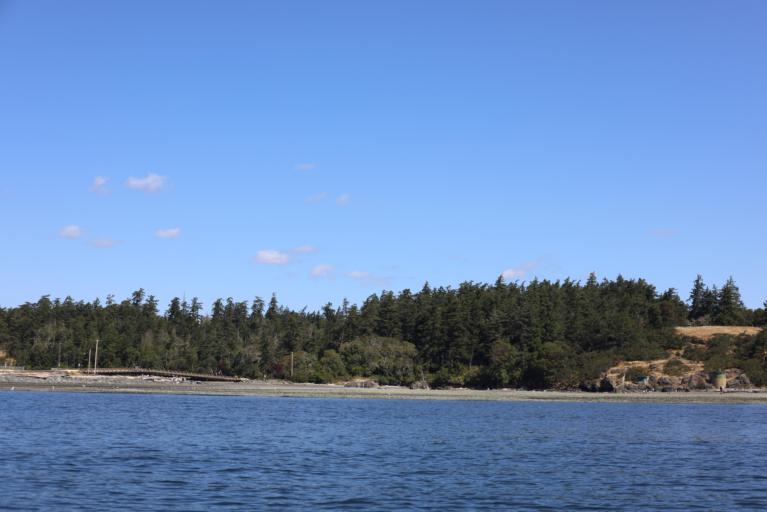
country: CA
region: British Columbia
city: Colwood
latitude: 48.4276
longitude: -123.4541
